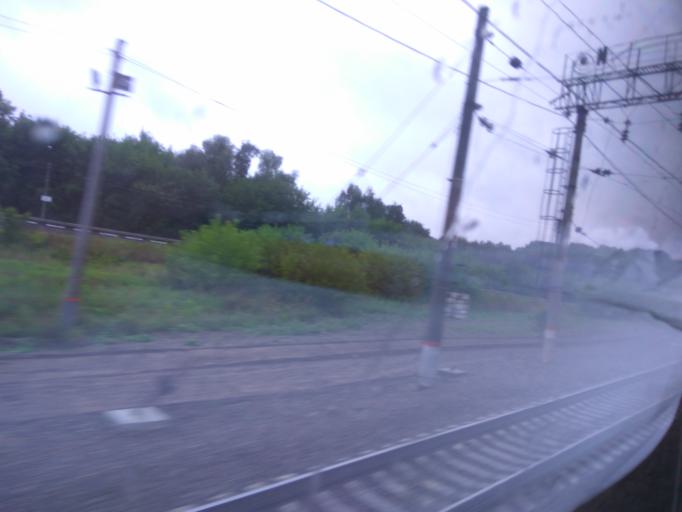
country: RU
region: Moskovskaya
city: Kashira
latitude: 54.8580
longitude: 38.2012
